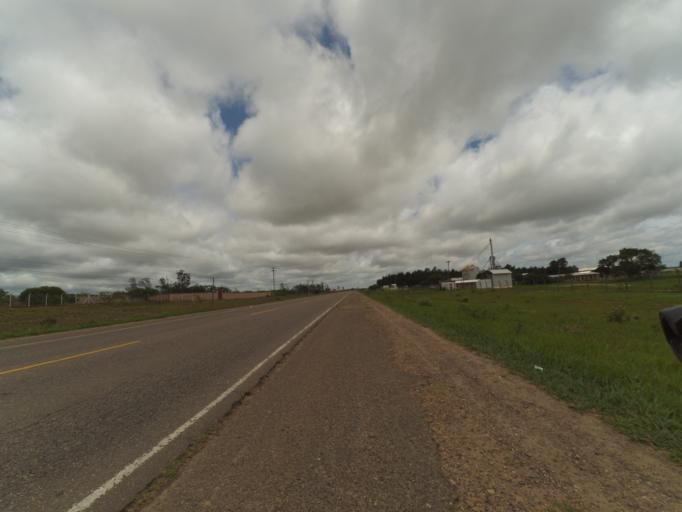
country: BO
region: Santa Cruz
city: Santa Rita
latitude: -17.9009
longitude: -63.2561
